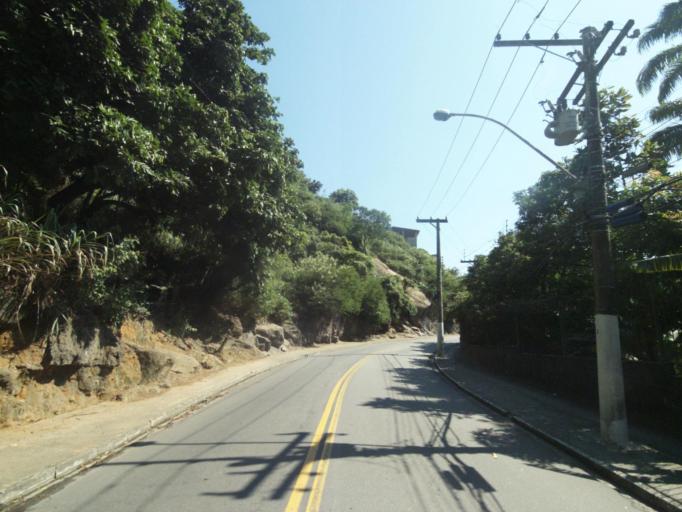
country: BR
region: Rio de Janeiro
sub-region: Niteroi
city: Niteroi
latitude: -22.9365
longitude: -43.1088
